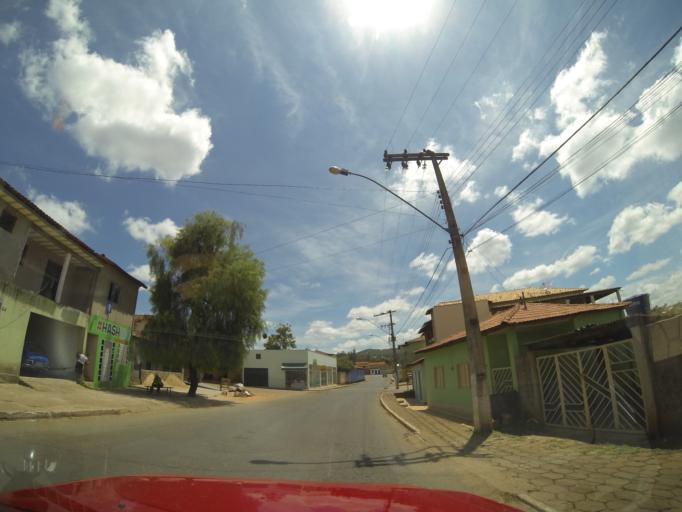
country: BR
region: Minas Gerais
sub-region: Diamantina
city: Diamantina
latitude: -18.0741
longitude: -43.4723
